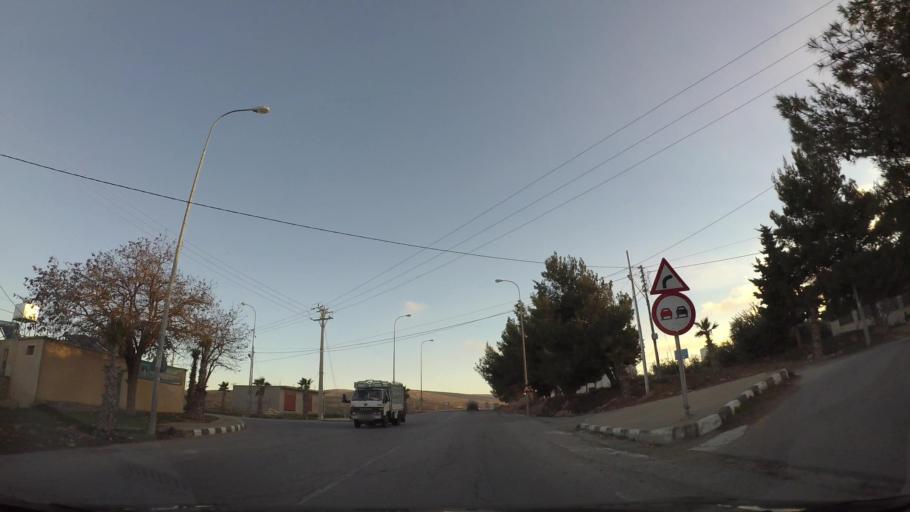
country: JO
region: Ma'an
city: Petra
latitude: 30.4521
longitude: 35.5255
